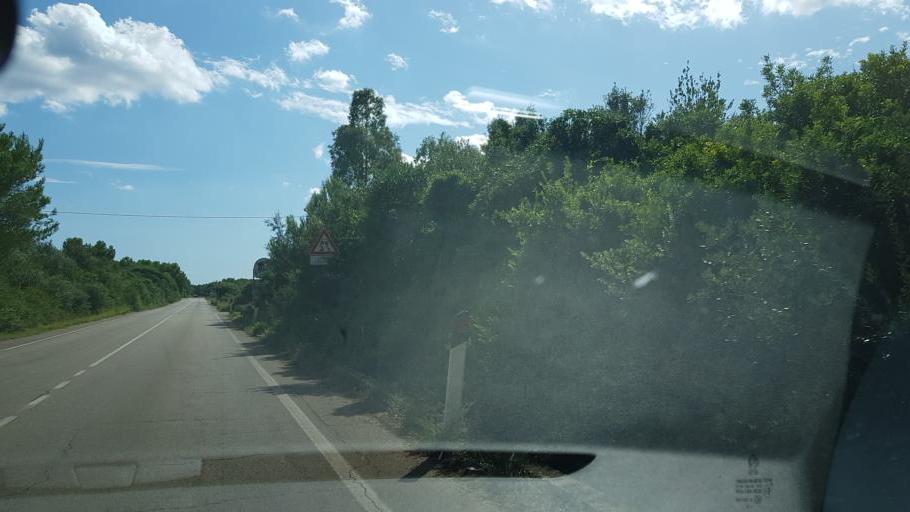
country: IT
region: Apulia
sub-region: Provincia di Lecce
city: Borgagne
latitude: 40.2457
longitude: 18.4419
